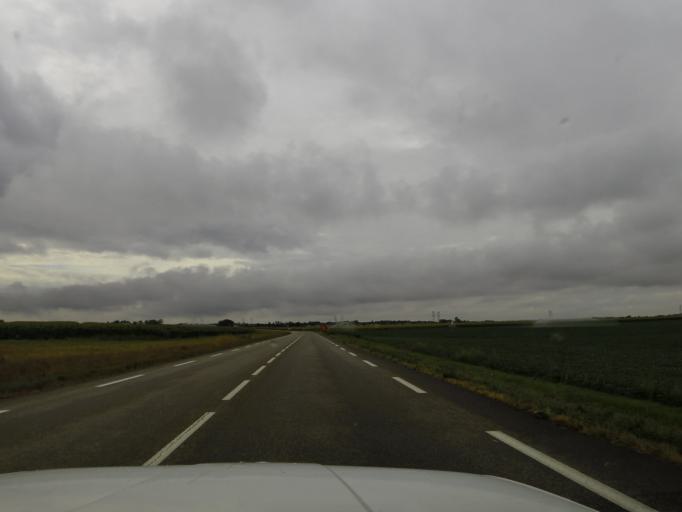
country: FR
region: Rhone-Alpes
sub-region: Departement de l'Ain
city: Perouges
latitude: 45.8754
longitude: 5.1822
